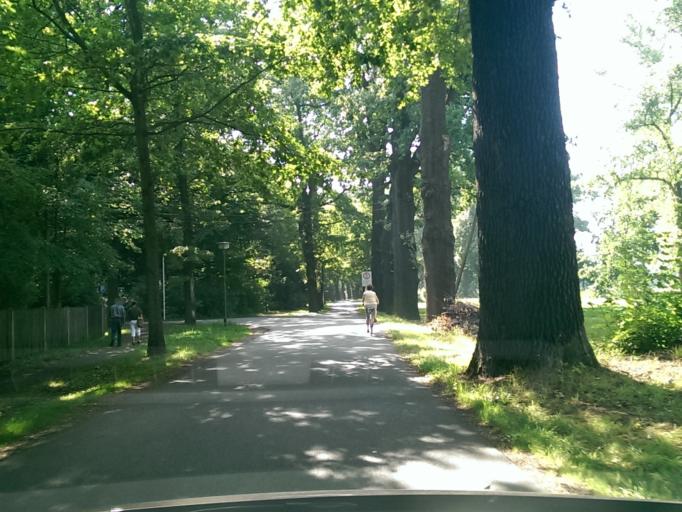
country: DE
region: Saxony
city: Zittau
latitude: 50.9010
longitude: 14.8310
